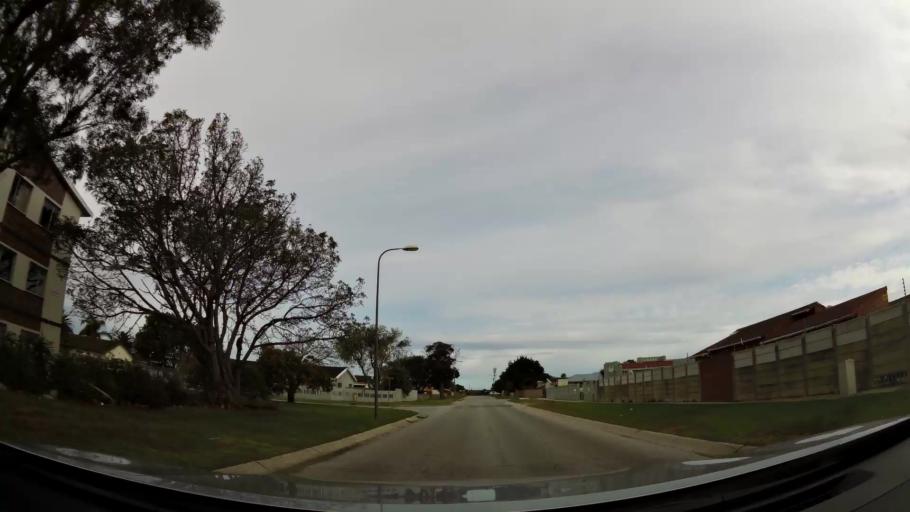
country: ZA
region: Eastern Cape
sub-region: Nelson Mandela Bay Metropolitan Municipality
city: Port Elizabeth
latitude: -33.9409
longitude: 25.4954
